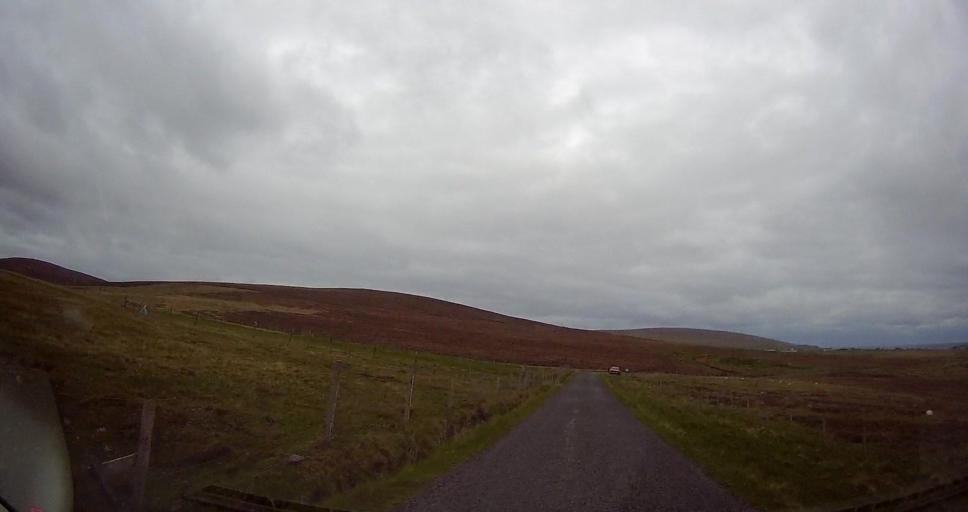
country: GB
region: Scotland
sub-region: Shetland Islands
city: Shetland
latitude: 60.7986
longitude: -0.8646
